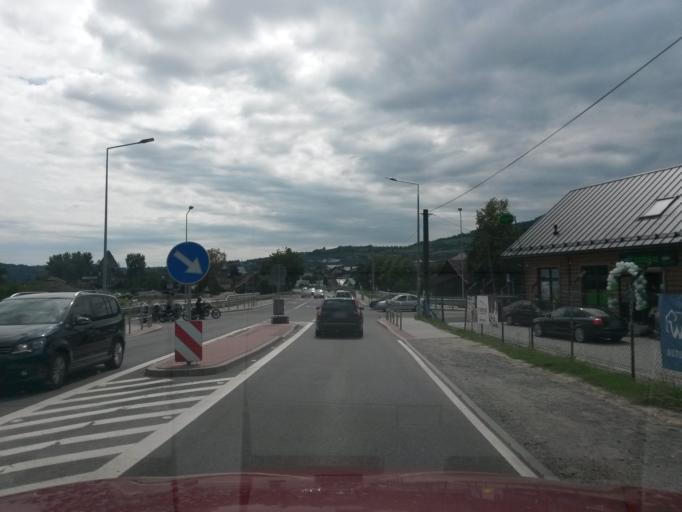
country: PL
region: Lesser Poland Voivodeship
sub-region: Powiat nowosadecki
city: Lososina Dolna
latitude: 49.7142
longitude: 20.6407
